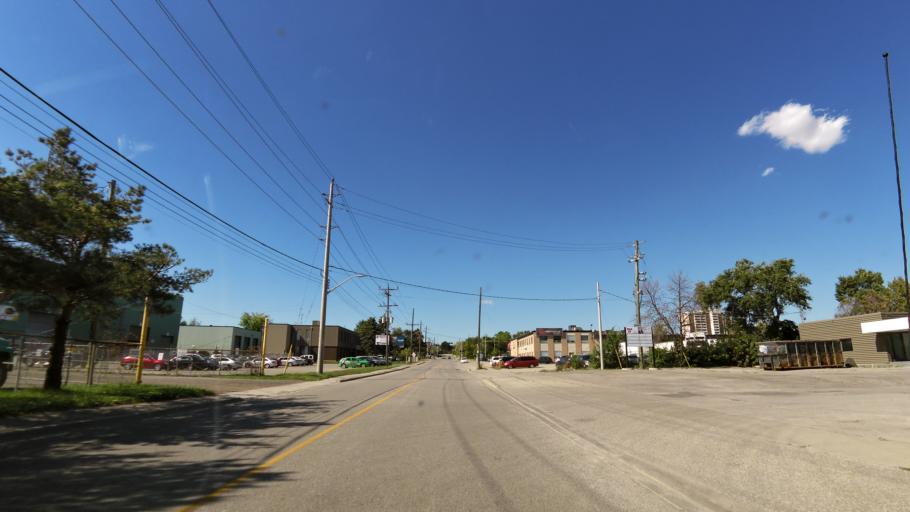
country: CA
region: Ontario
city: Etobicoke
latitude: 43.5953
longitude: -79.5935
